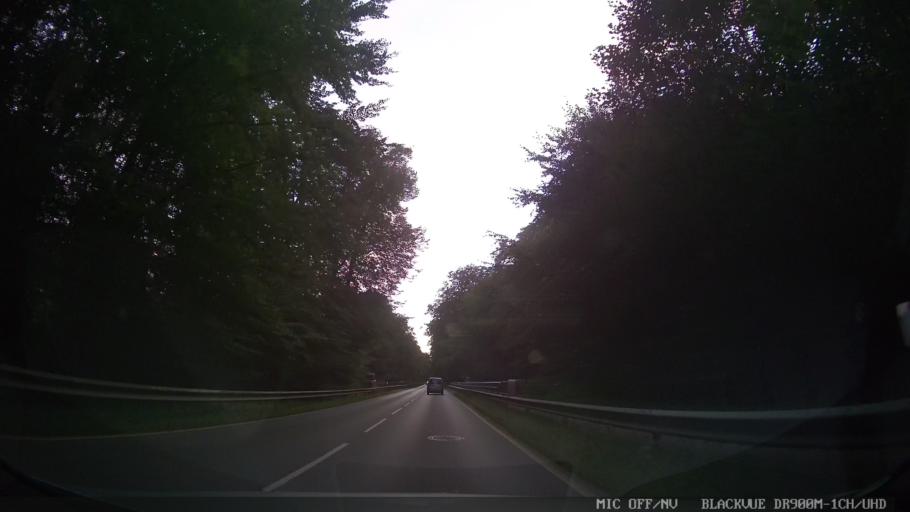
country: DE
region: Schleswig-Holstein
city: Ratekau
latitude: 53.9325
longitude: 10.7181
